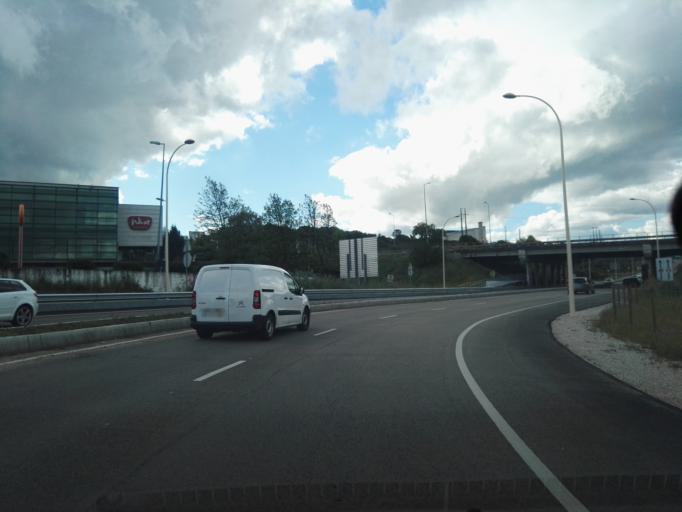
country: PT
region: Santarem
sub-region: Torres Novas
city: Torres Novas
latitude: 39.4641
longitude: -8.5309
